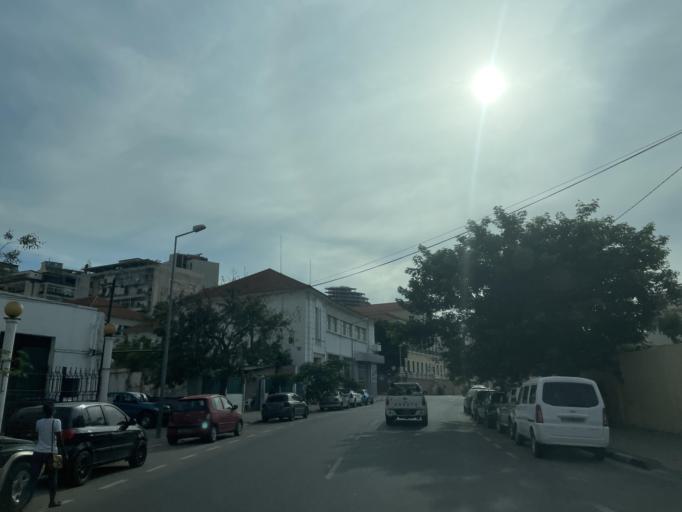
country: AO
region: Luanda
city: Luanda
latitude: -8.8129
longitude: 13.2354
